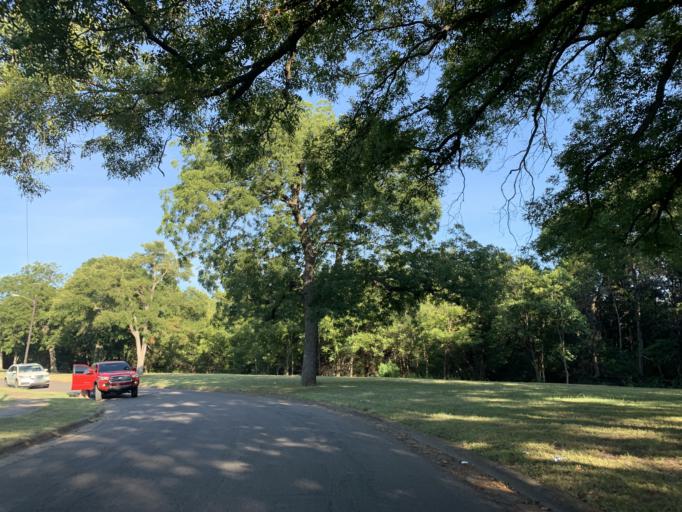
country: US
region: Texas
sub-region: Dallas County
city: Cockrell Hill
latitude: 32.7094
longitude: -96.8989
